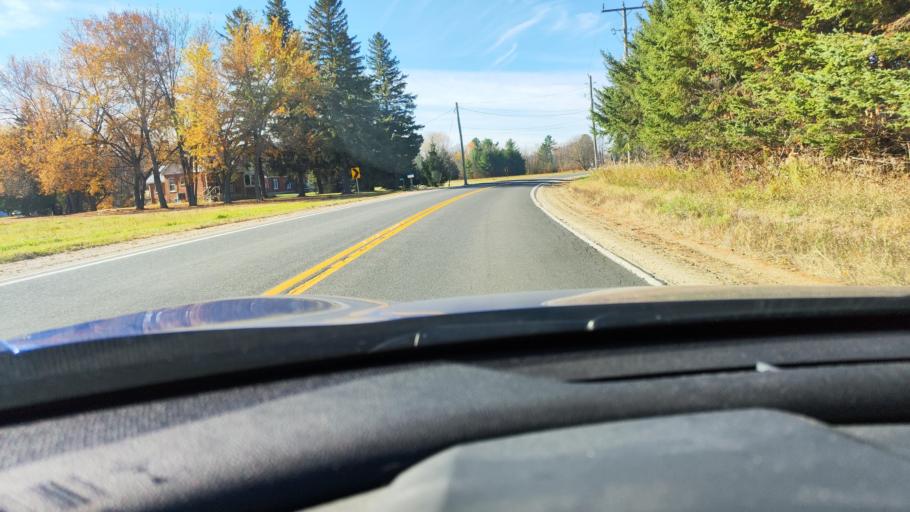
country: CA
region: Ontario
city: Angus
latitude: 44.3437
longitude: -80.0170
